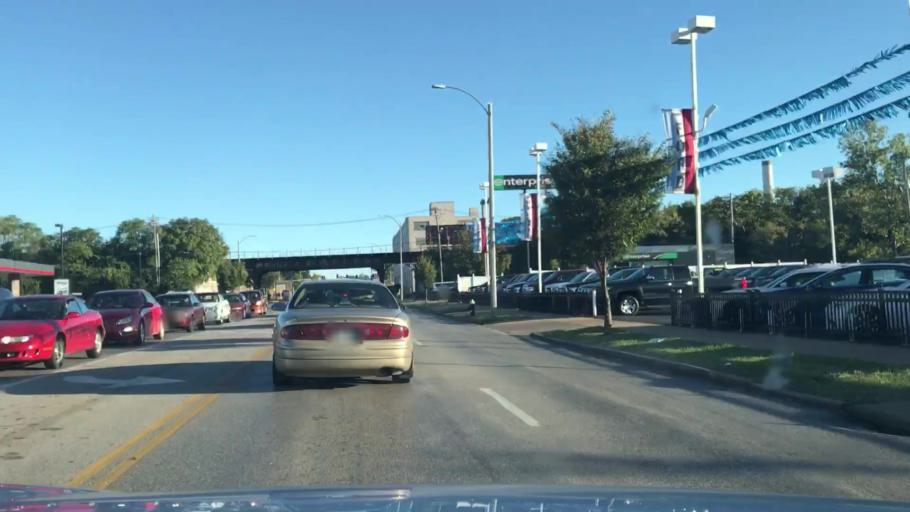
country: US
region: Missouri
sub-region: Saint Louis County
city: Maplewood
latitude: 38.5999
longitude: -90.2702
